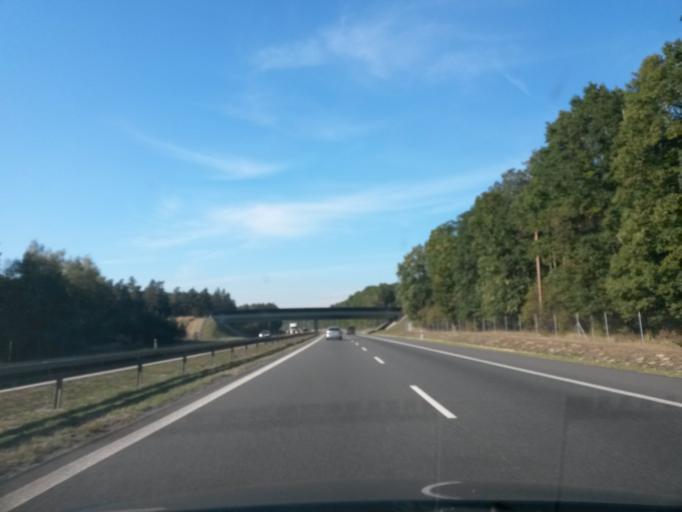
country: PL
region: Opole Voivodeship
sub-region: Powiat opolski
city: Proszkow
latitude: 50.5486
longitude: 17.8930
